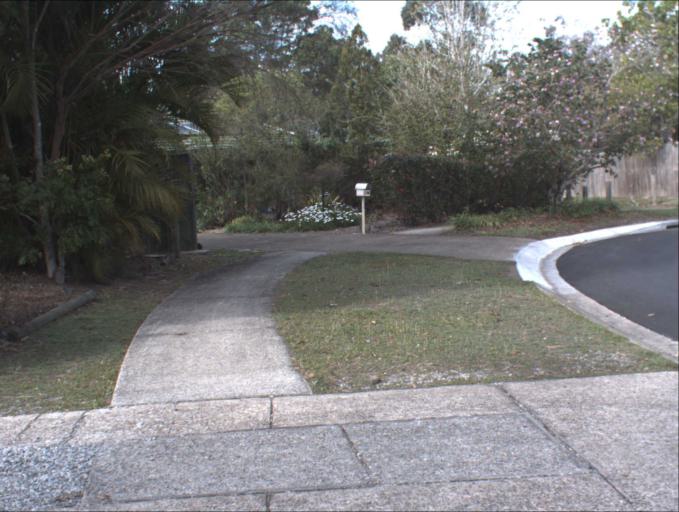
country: AU
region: Queensland
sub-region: Logan
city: Woodridge
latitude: -27.6684
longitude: 153.0649
